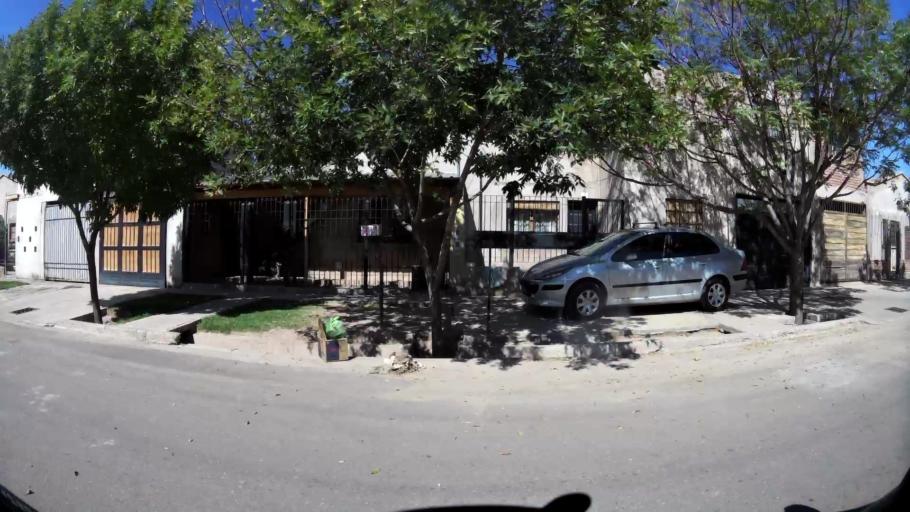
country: AR
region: Mendoza
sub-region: Departamento de Godoy Cruz
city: Godoy Cruz
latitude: -32.9556
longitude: -68.8256
